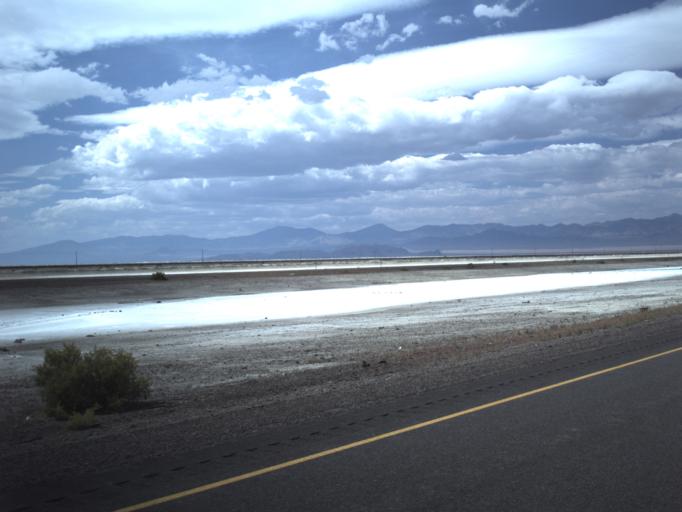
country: US
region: Utah
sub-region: Tooele County
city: Wendover
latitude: 40.7407
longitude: -113.9174
